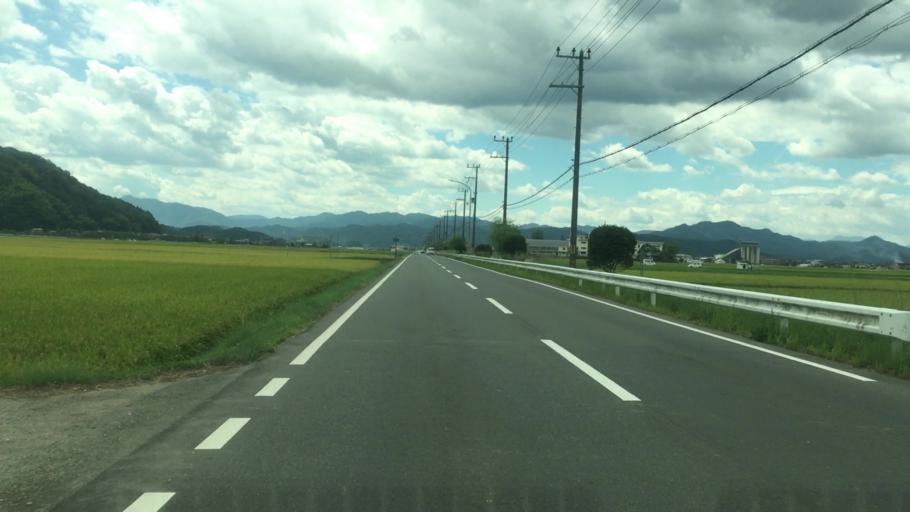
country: JP
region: Hyogo
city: Toyooka
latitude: 35.5361
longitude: 134.8397
